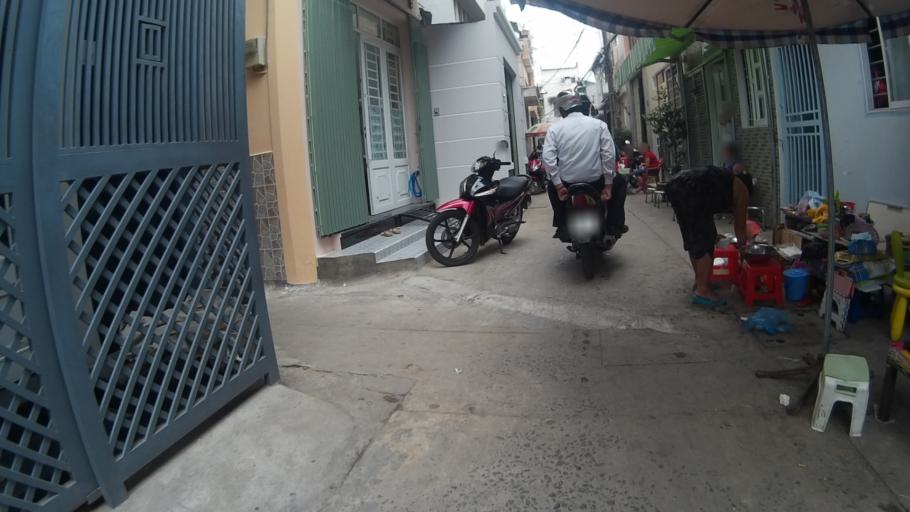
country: VN
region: Ho Chi Minh City
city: Quan Ba
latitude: 10.7607
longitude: 106.6870
